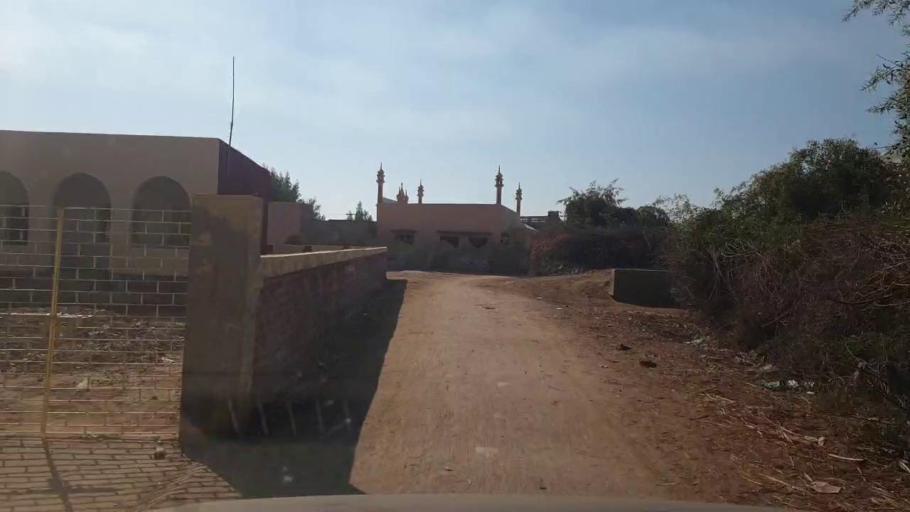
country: PK
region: Sindh
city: Mirwah Gorchani
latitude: 25.2994
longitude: 69.0941
